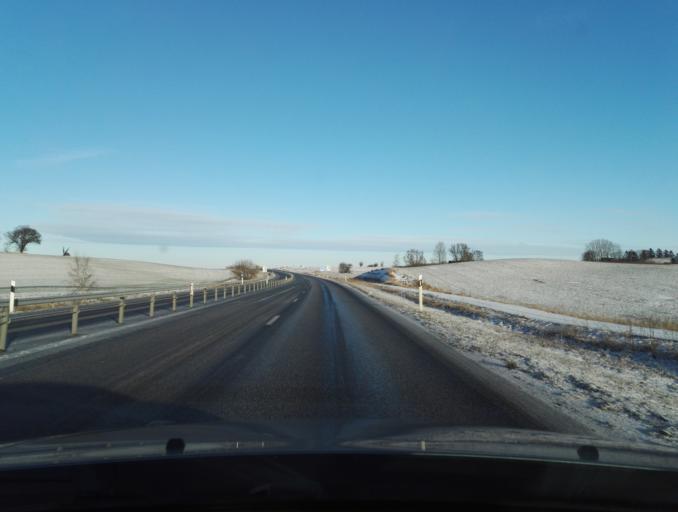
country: SE
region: Skane
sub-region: Svedala Kommun
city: Svedala
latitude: 55.4883
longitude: 13.2345
